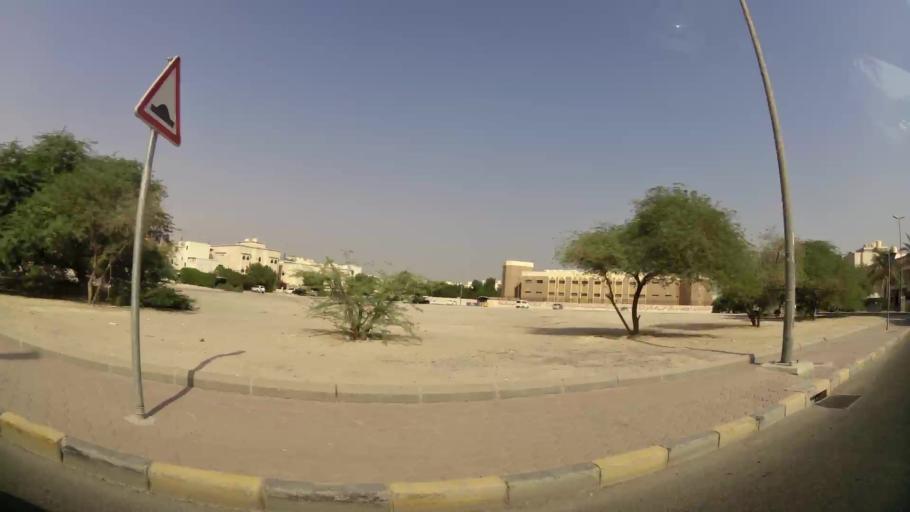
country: KW
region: Al Asimah
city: Ar Rabiyah
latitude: 29.2710
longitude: 47.8826
